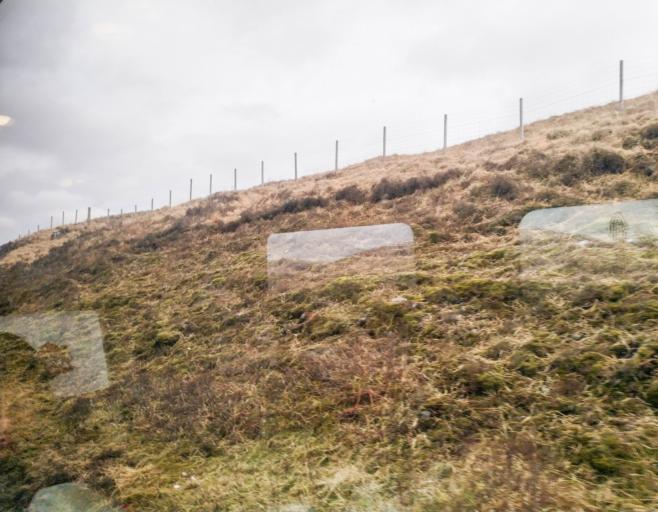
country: GB
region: Scotland
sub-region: Highland
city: Spean Bridge
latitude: 56.5361
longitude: -4.7623
